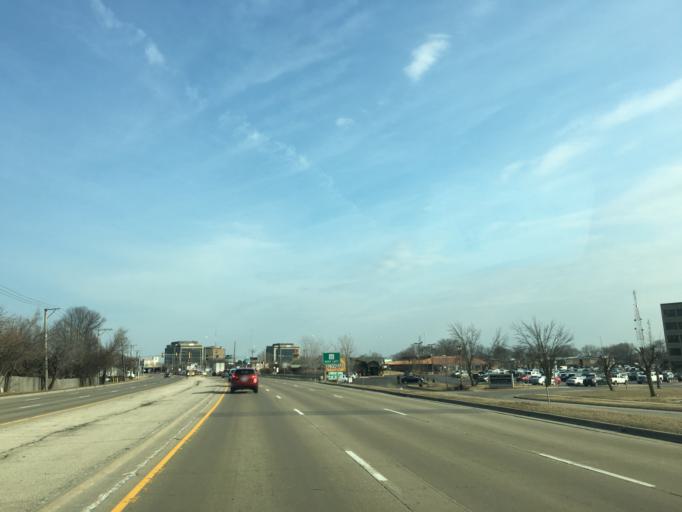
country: US
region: Illinois
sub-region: Cook County
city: Rolling Meadows
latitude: 42.0646
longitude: -88.0351
